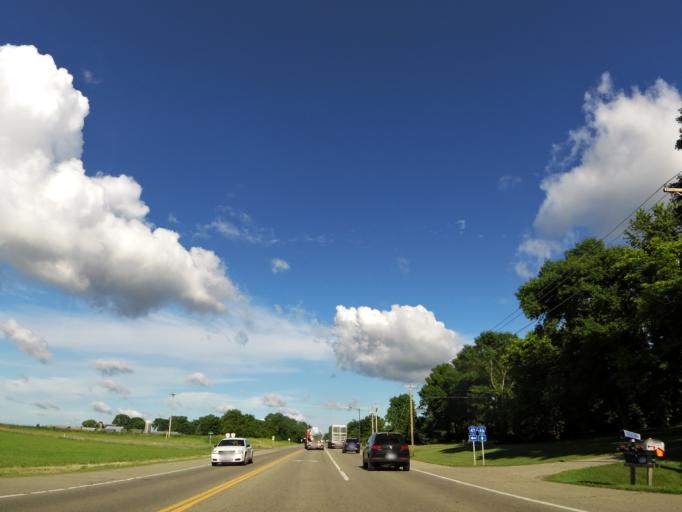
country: US
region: Minnesota
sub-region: Dakota County
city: Hastings
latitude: 44.7168
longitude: -92.8869
